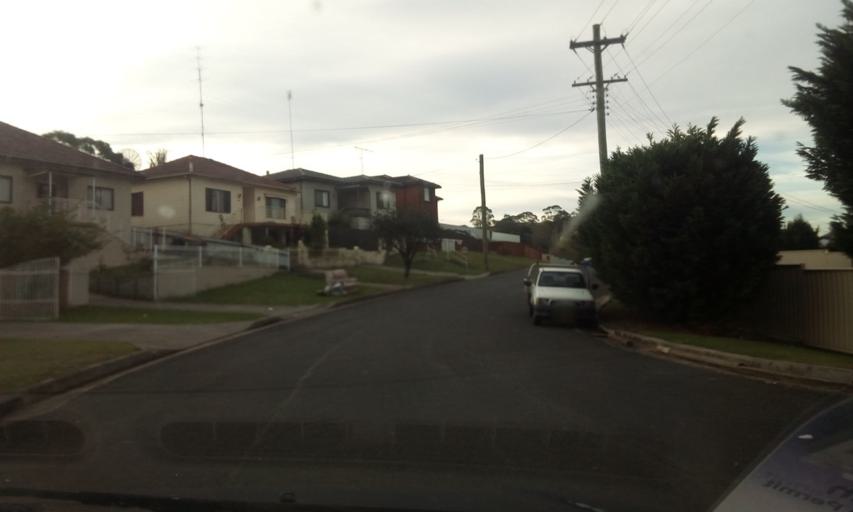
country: AU
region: New South Wales
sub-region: Wollongong
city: Lake Heights
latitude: -34.4763
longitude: 150.8707
